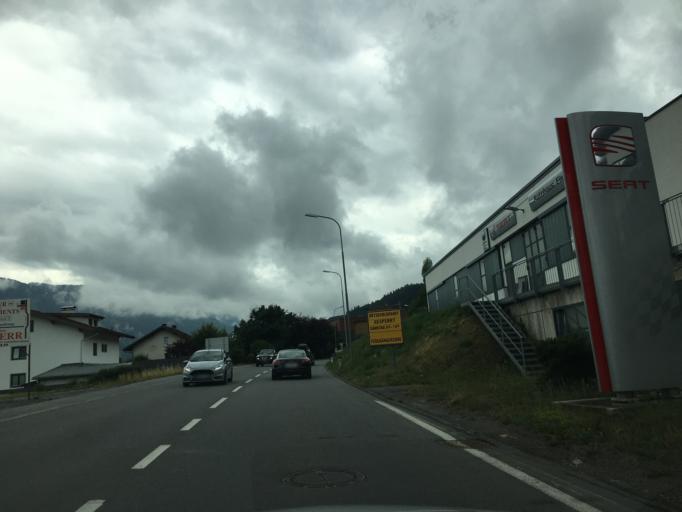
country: AT
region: Tyrol
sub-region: Politischer Bezirk Imst
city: Imst
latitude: 47.2473
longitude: 10.7445
